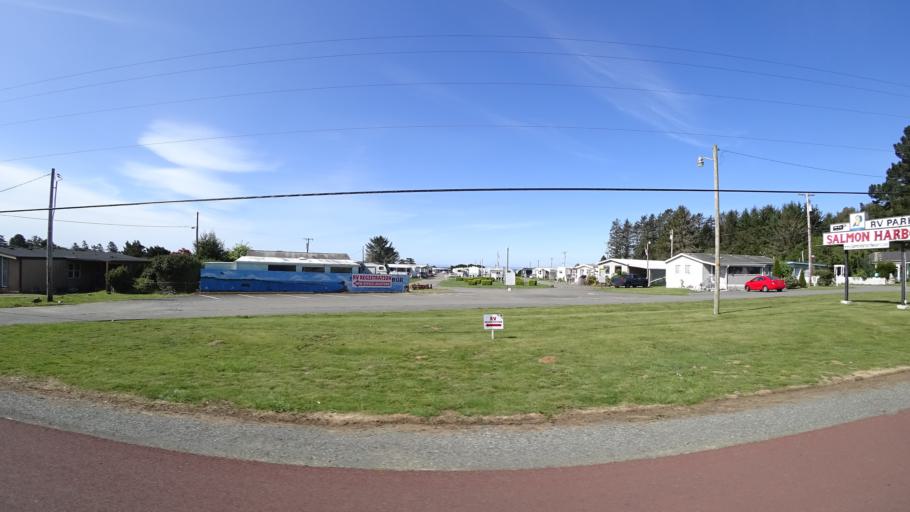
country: US
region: Oregon
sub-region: Curry County
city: Harbor
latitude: 41.9481
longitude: -124.1974
